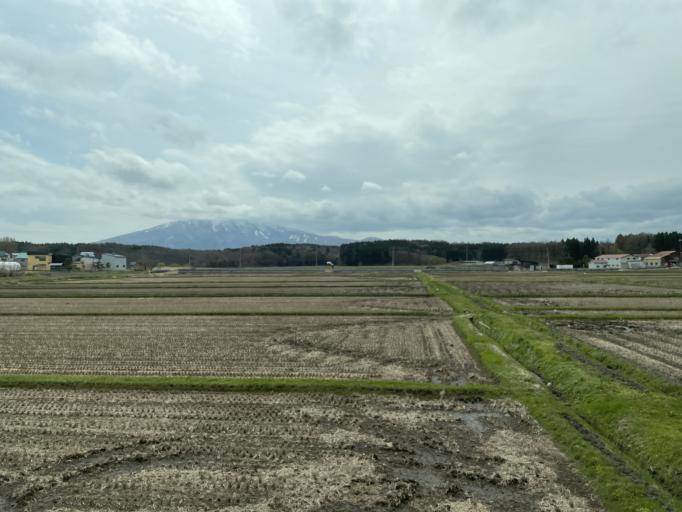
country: JP
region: Aomori
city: Shimokizukuri
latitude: 40.7856
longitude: 140.3128
